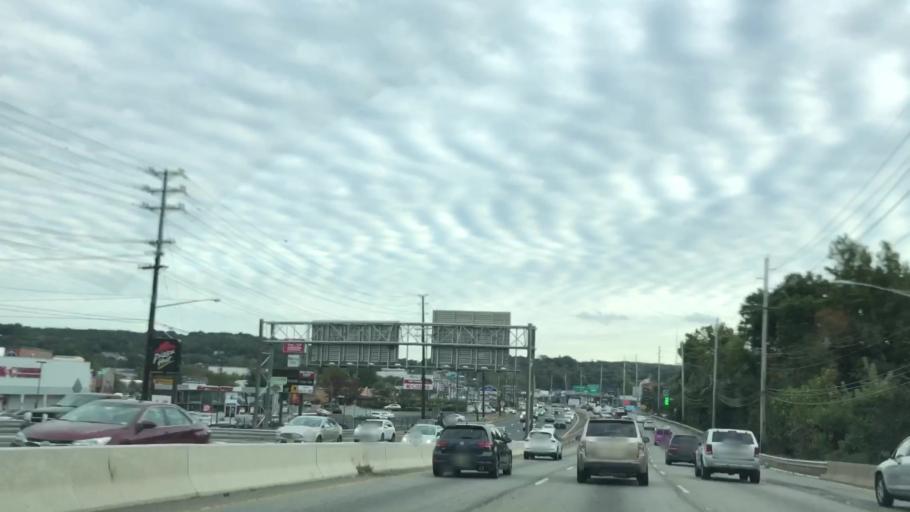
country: US
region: New Jersey
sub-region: Passaic County
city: Totowa
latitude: 40.8888
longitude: -74.2183
